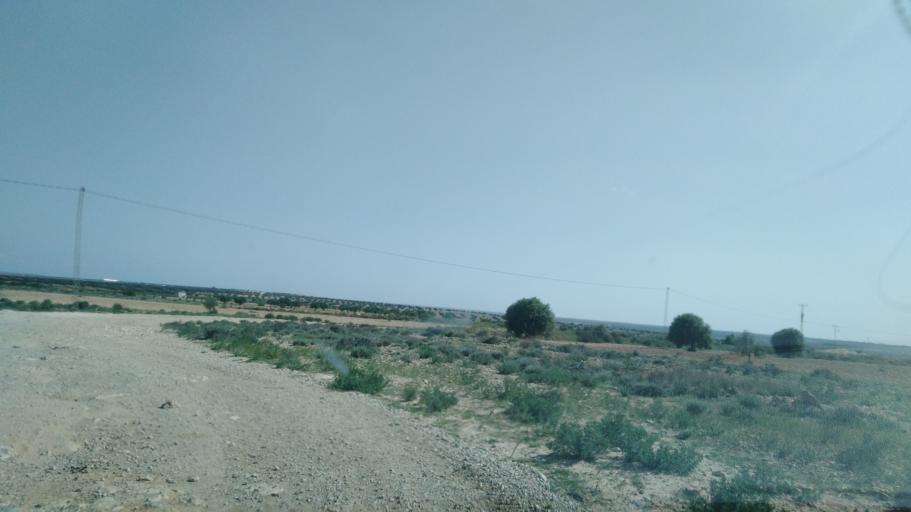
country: TN
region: Safaqis
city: Bi'r `Ali Bin Khalifah
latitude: 34.7968
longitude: 10.3743
